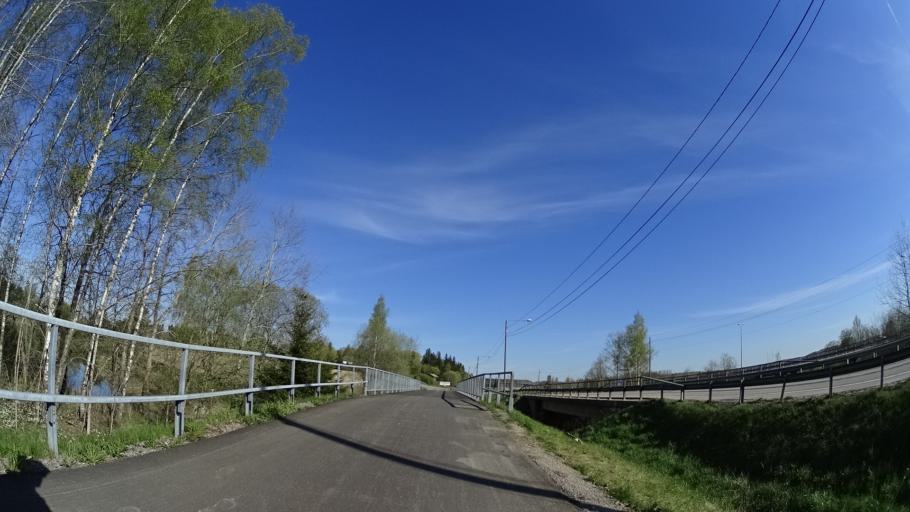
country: FI
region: Uusimaa
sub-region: Helsinki
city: Nurmijaervi
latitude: 60.3422
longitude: 24.8130
